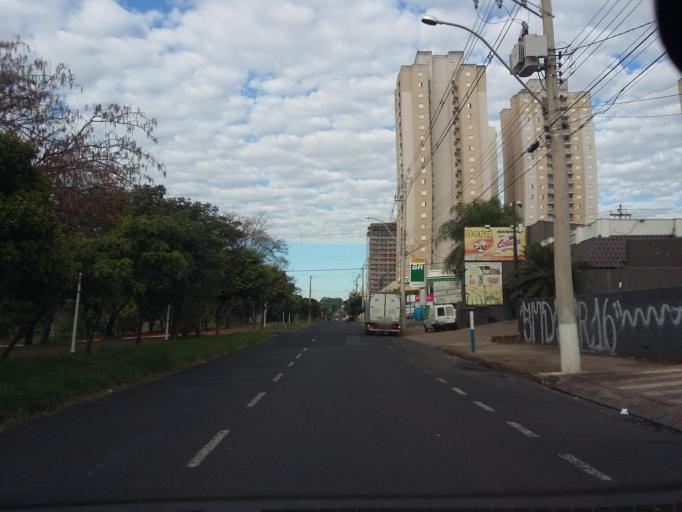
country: BR
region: Sao Paulo
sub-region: Sao Jose Do Rio Preto
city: Sao Jose do Rio Preto
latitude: -20.8357
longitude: -49.4080
